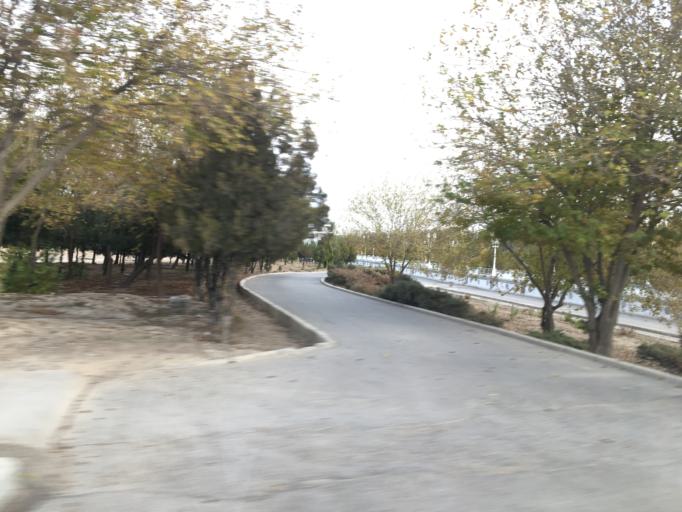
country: TM
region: Ahal
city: Ashgabat
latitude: 37.9060
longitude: 58.4059
